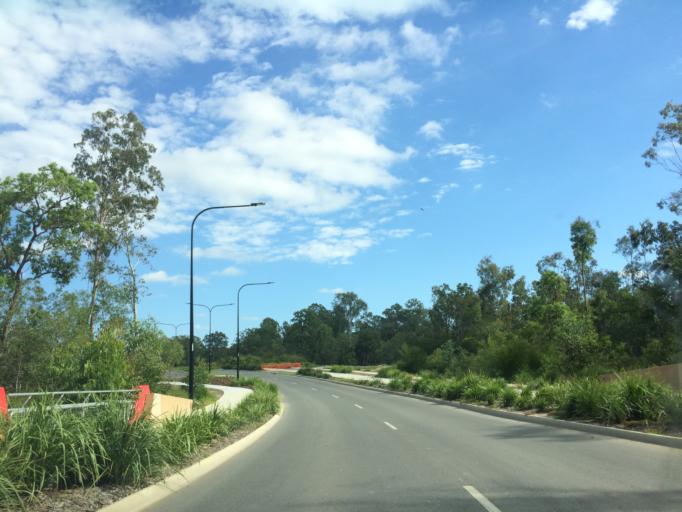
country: AU
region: Queensland
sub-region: Logan
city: North Maclean
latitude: -27.8046
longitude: 152.9464
